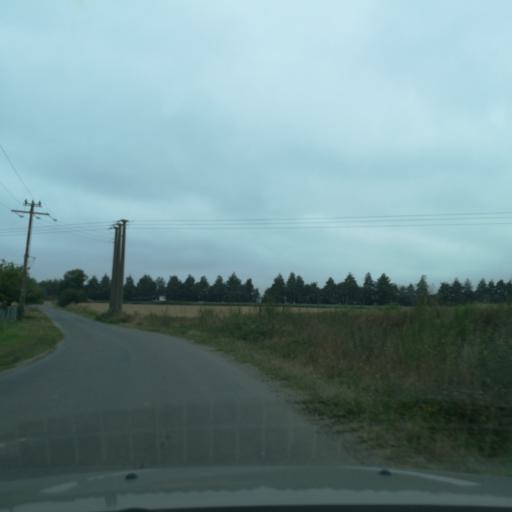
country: FR
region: Brittany
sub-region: Departement d'Ille-et-Vilaine
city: Montauban-de-Bretagne
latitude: 48.1877
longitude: -2.0184
